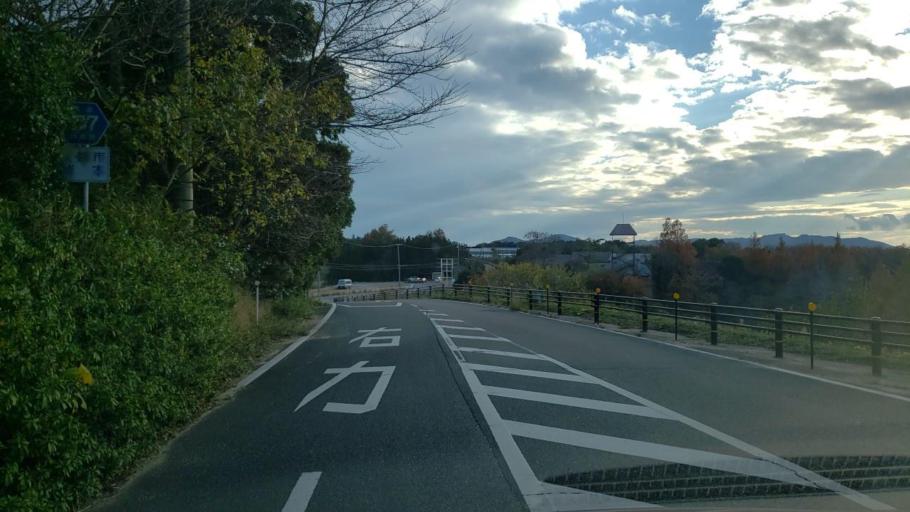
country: JP
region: Hyogo
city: Akashi
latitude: 34.5628
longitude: 134.9760
